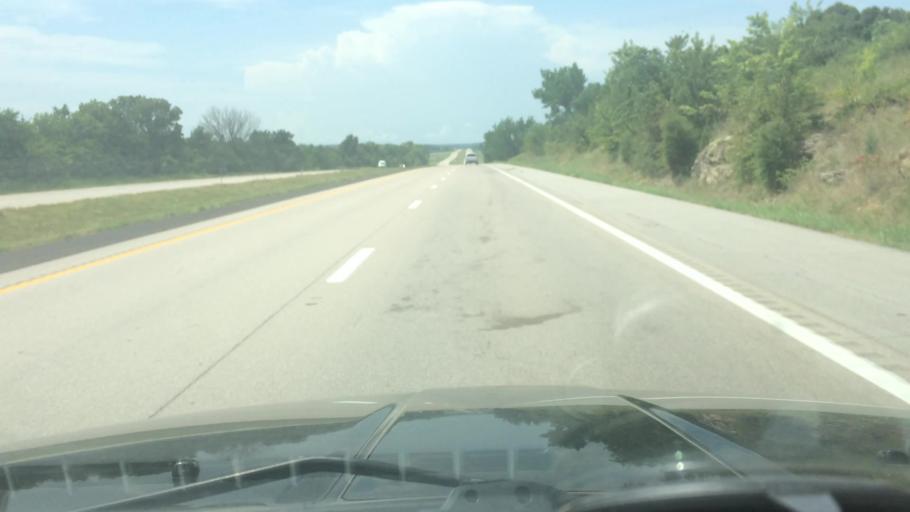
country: US
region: Missouri
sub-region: Polk County
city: Humansville
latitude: 37.7810
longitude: -93.5756
